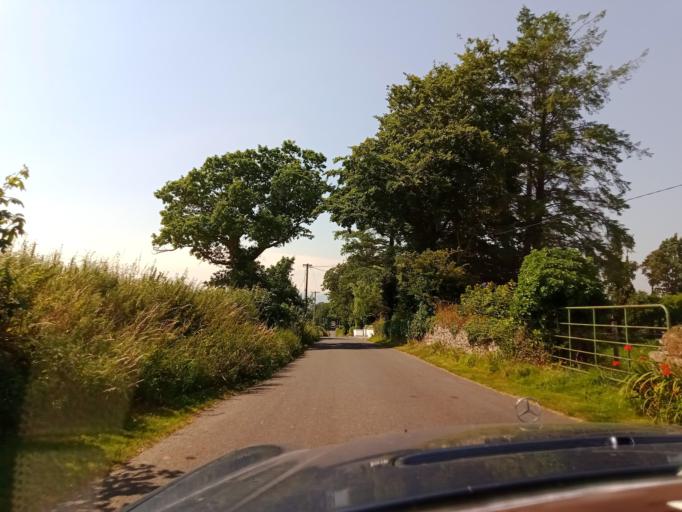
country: IE
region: Leinster
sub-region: Kilkenny
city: Piltown
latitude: 52.3384
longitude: -7.3095
